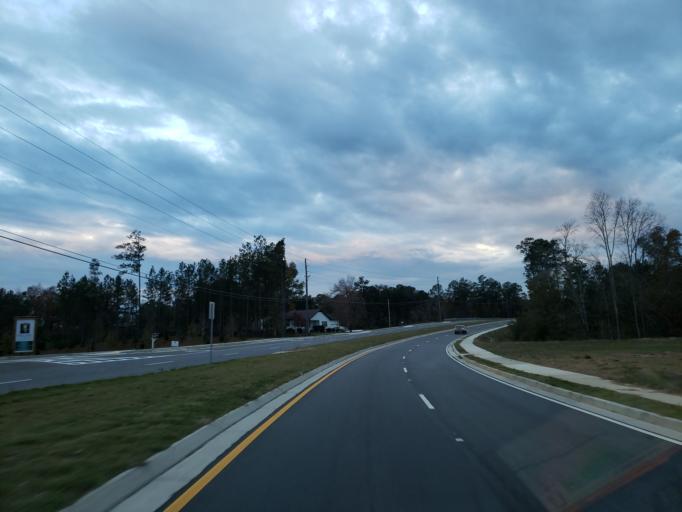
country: US
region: Georgia
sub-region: Cobb County
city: Acworth
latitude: 34.0578
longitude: -84.7338
